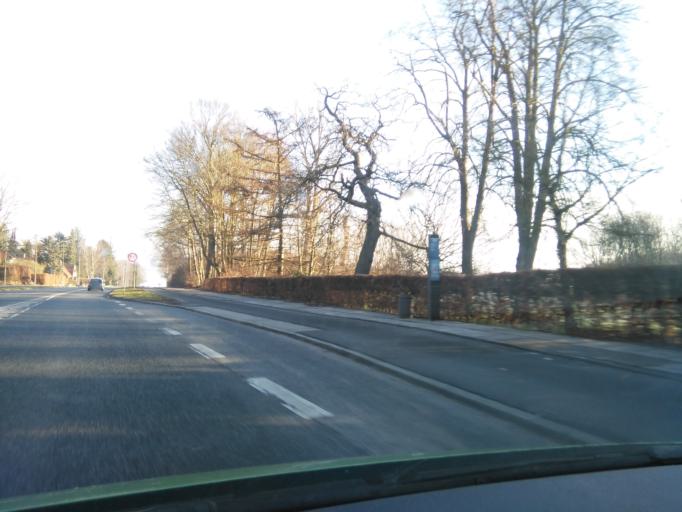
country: DK
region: Central Jutland
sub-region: Arhus Kommune
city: Arhus
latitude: 56.1252
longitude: 10.2088
